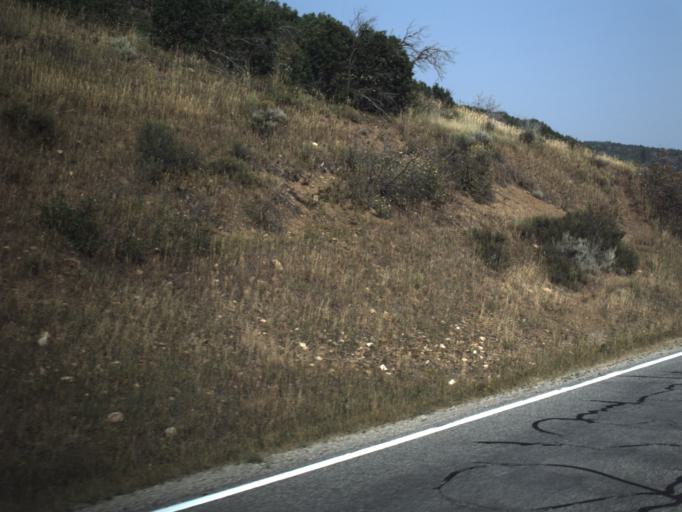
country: US
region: Utah
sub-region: Summit County
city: Kamas
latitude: 40.6281
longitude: -111.1670
